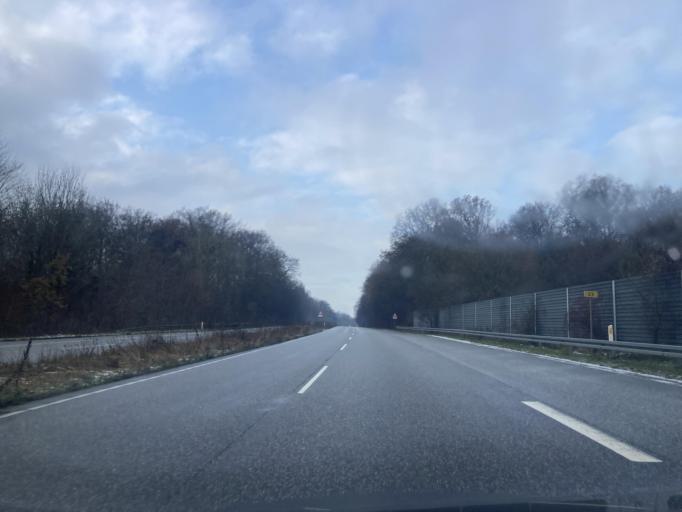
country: DK
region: Zealand
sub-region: Holbaek Kommune
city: Jyderup
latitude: 55.6636
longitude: 11.4042
